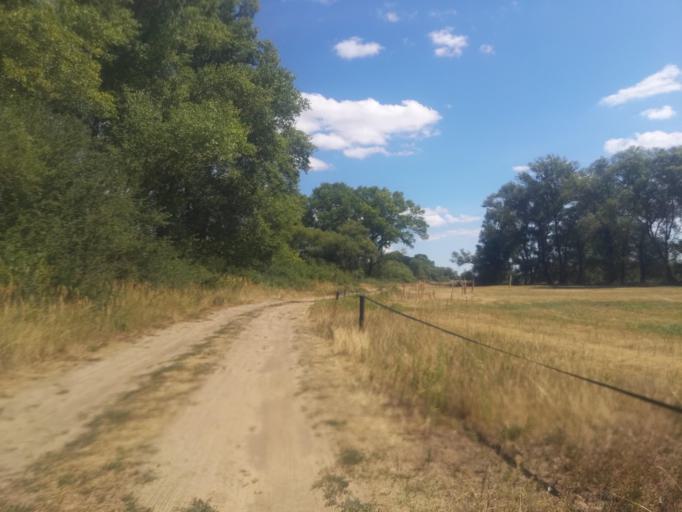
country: DE
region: Lower Saxony
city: Neu Darchau
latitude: 53.2526
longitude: 10.8454
